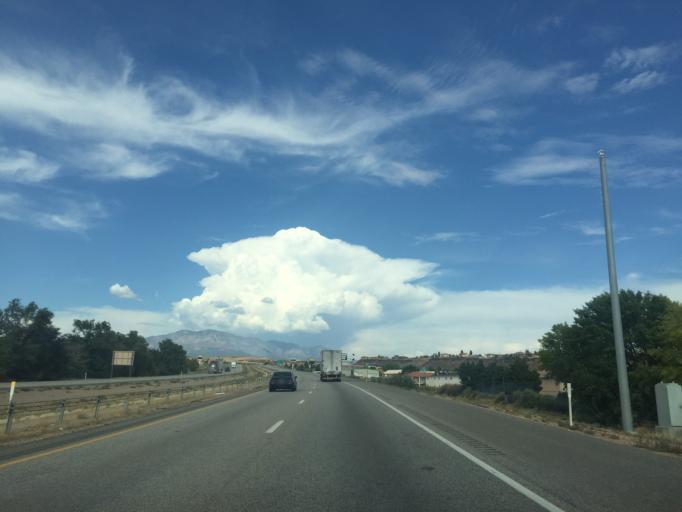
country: US
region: Utah
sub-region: Washington County
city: Saint George
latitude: 37.1002
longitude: -113.5619
